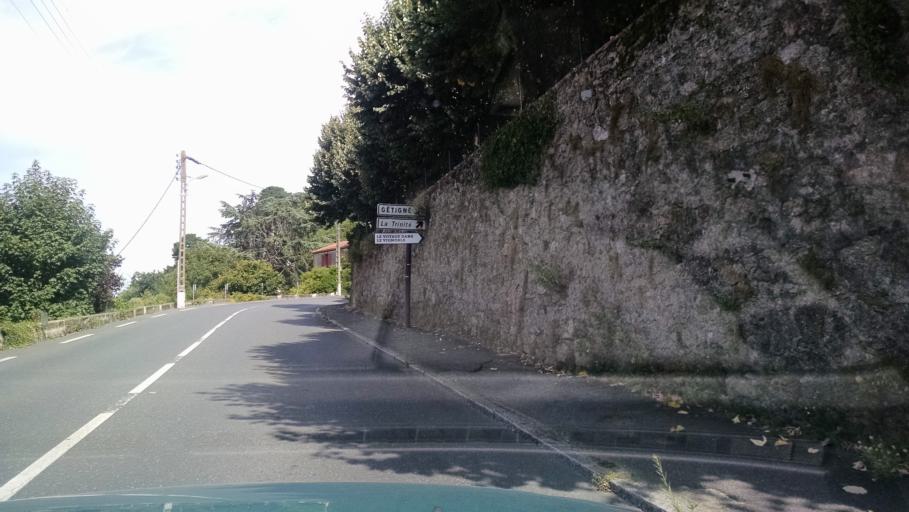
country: FR
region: Pays de la Loire
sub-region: Departement de la Loire-Atlantique
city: Clisson
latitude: 47.0914
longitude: -1.2813
